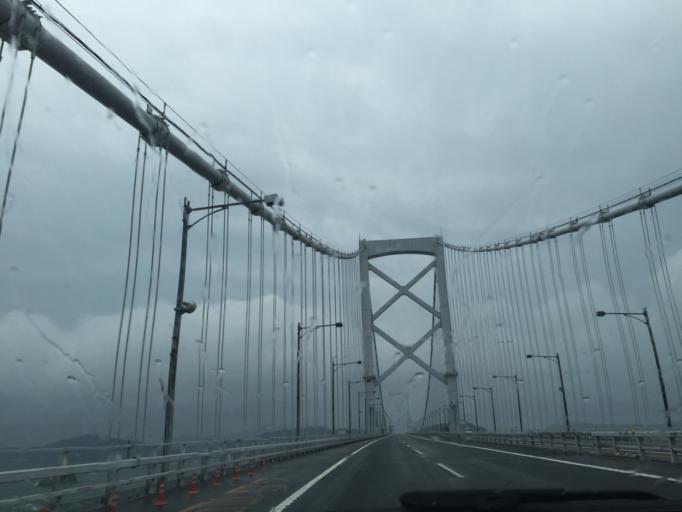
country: JP
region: Hyogo
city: Fukura
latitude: 34.2407
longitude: 134.6577
